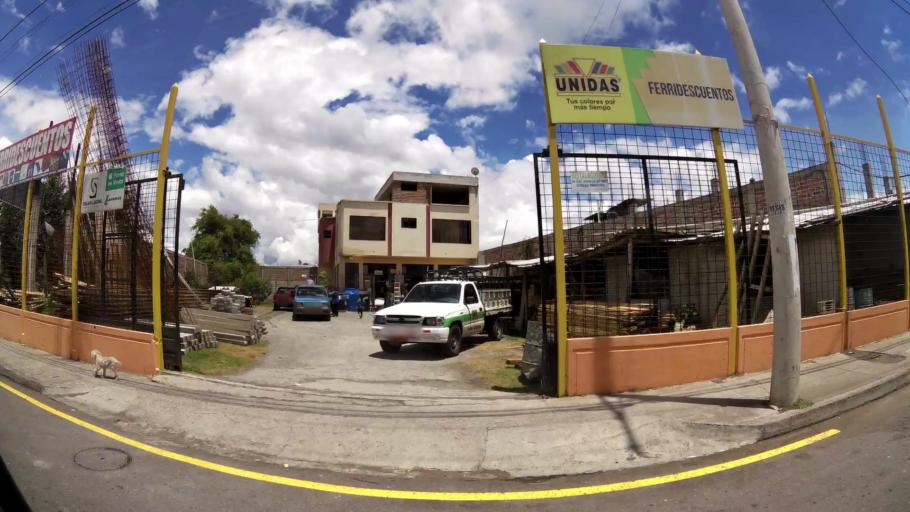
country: EC
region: Tungurahua
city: Ambato
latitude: -1.3027
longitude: -78.6018
